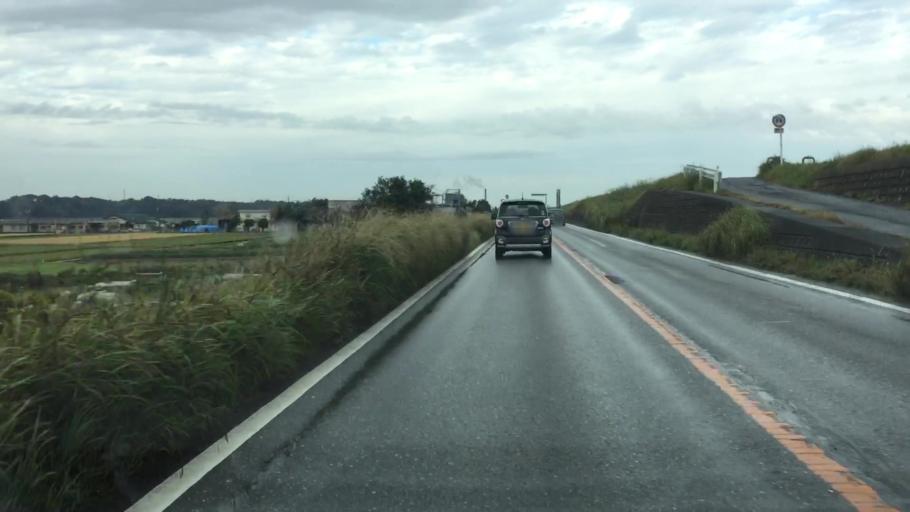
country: JP
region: Ibaraki
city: Toride
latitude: 35.8722
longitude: 140.1131
